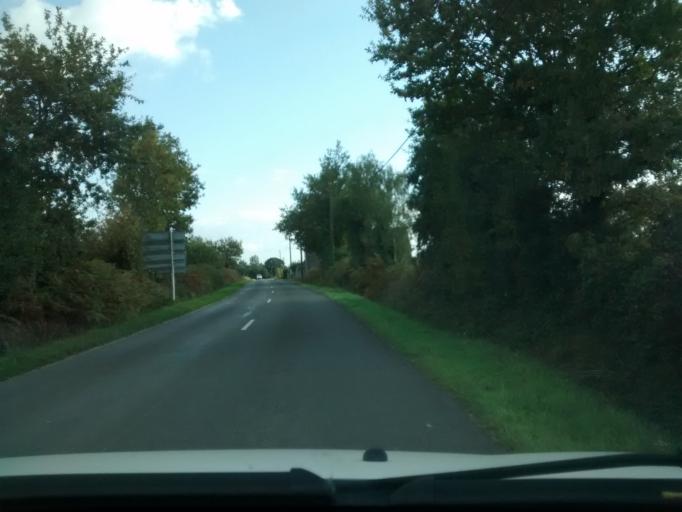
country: FR
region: Pays de la Loire
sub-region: Departement de la Loire-Atlantique
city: Sautron
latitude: 47.2889
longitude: -1.6563
